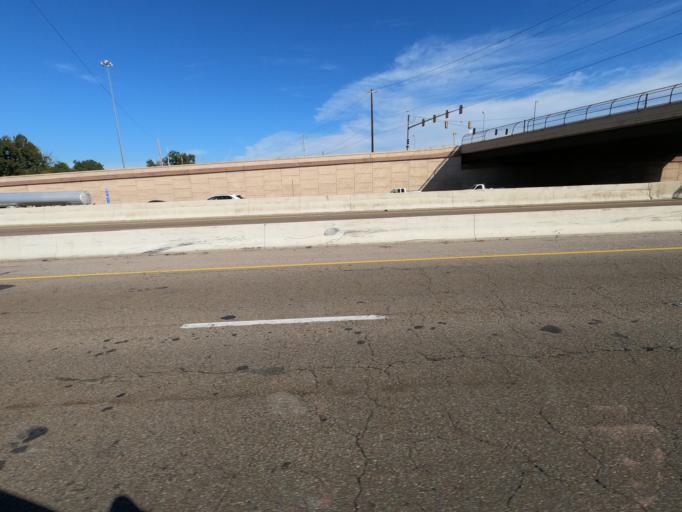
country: US
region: Tennessee
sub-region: Shelby County
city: Memphis
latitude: 35.1584
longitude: -90.0215
